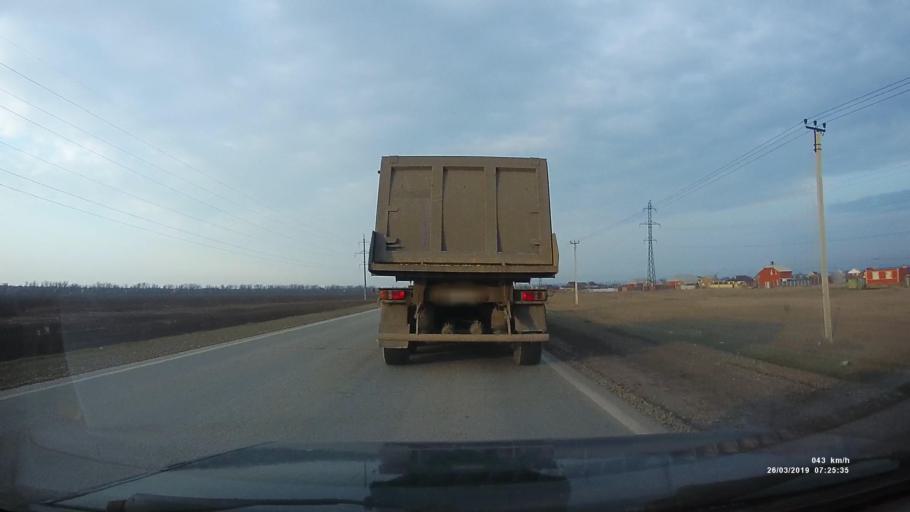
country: RU
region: Rostov
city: Taganrog
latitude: 47.2707
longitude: 38.8474
